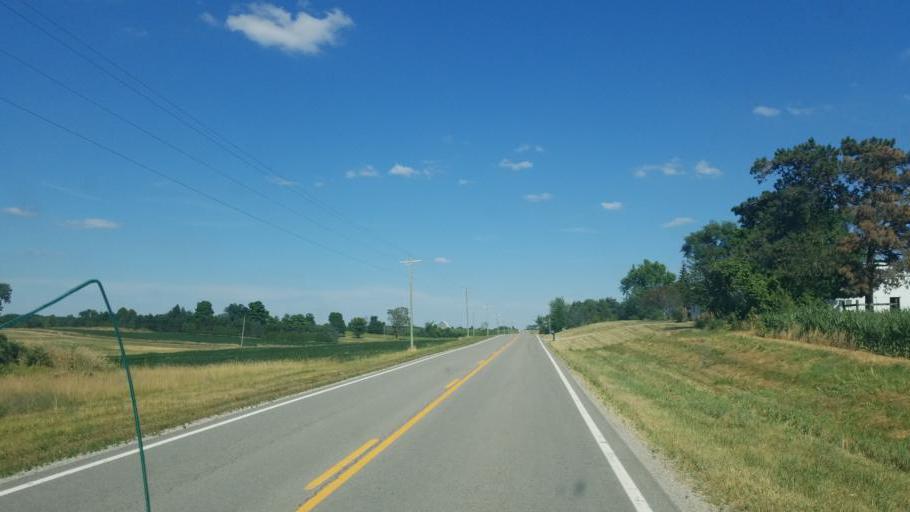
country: US
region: Ohio
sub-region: Williams County
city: Edgerton
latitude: 41.3825
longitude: -84.7820
